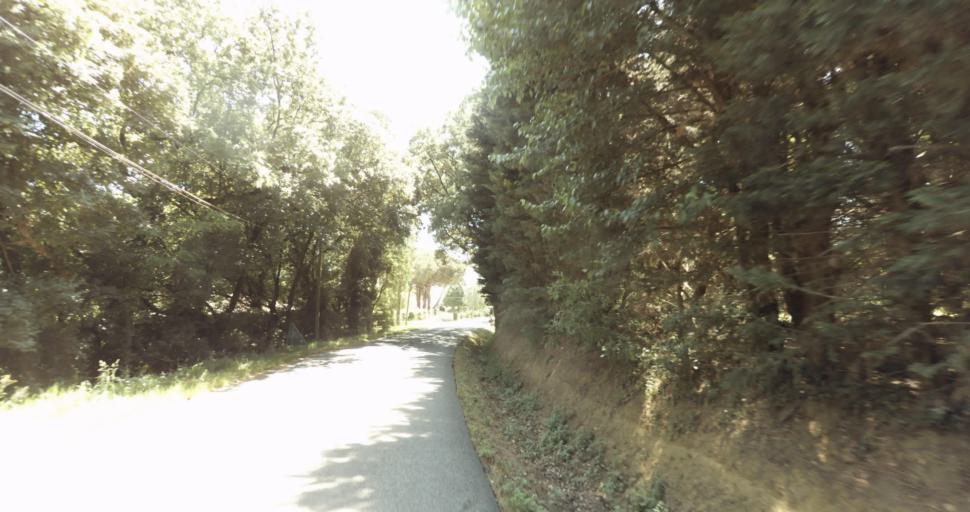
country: FR
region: Midi-Pyrenees
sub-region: Departement de la Haute-Garonne
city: Levignac
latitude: 43.6453
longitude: 1.1756
